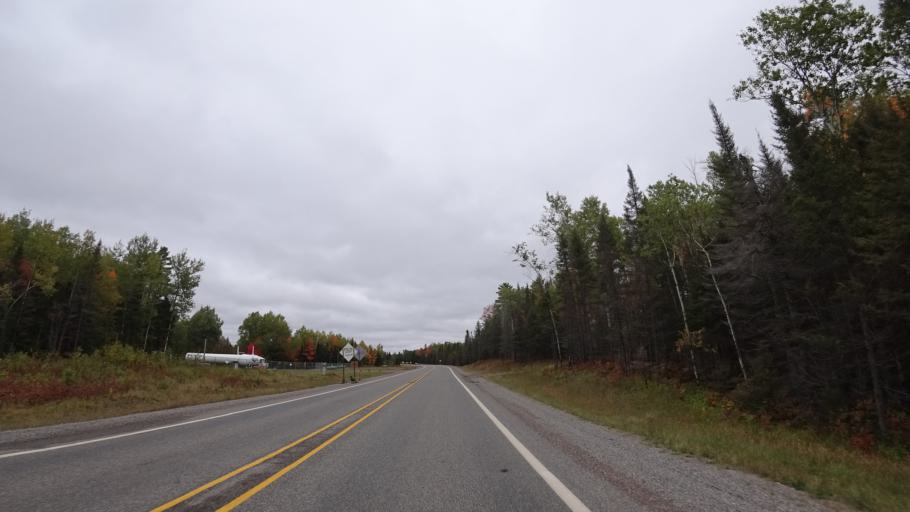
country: US
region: Michigan
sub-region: Marquette County
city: West Ishpeming
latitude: 46.4890
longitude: -87.9199
